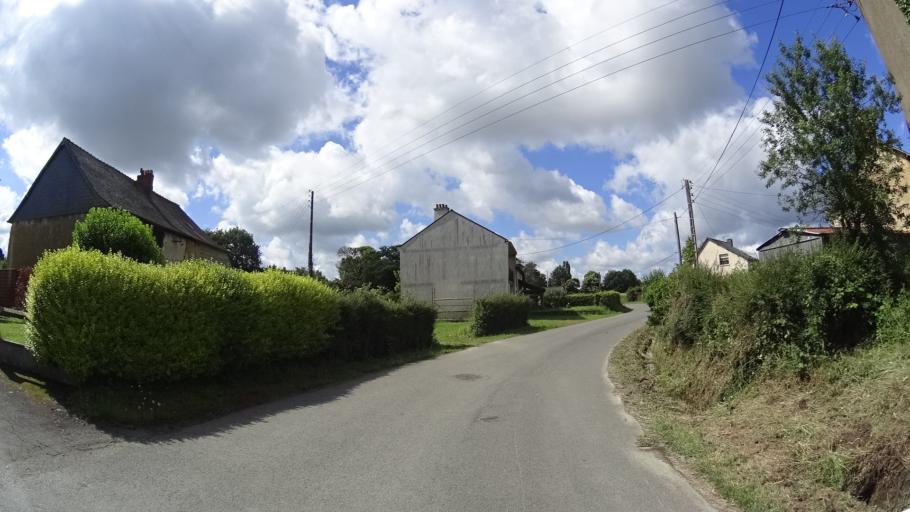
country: FR
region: Brittany
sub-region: Departement d'Ille-et-Vilaine
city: Le Rheu
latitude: 48.1186
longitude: -1.8049
